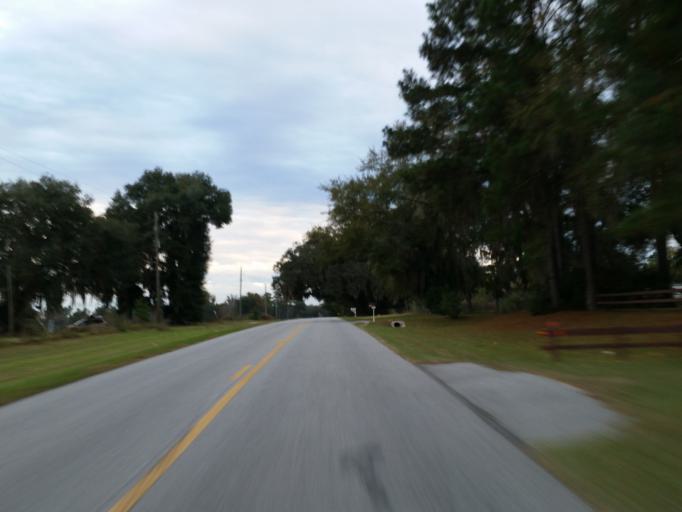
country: US
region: Florida
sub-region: Hamilton County
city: Jasper
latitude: 30.5385
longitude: -83.1026
